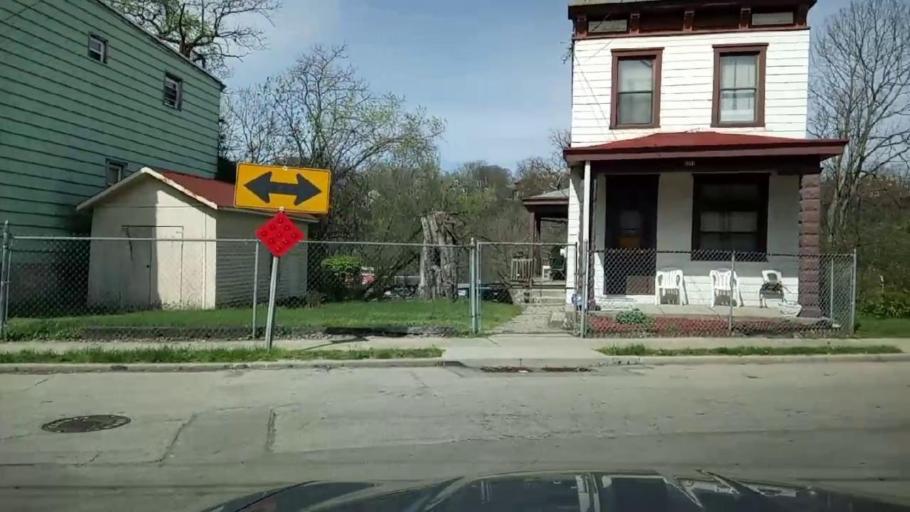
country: US
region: Kentucky
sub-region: Campbell County
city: Newport
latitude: 39.1223
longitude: -84.5130
